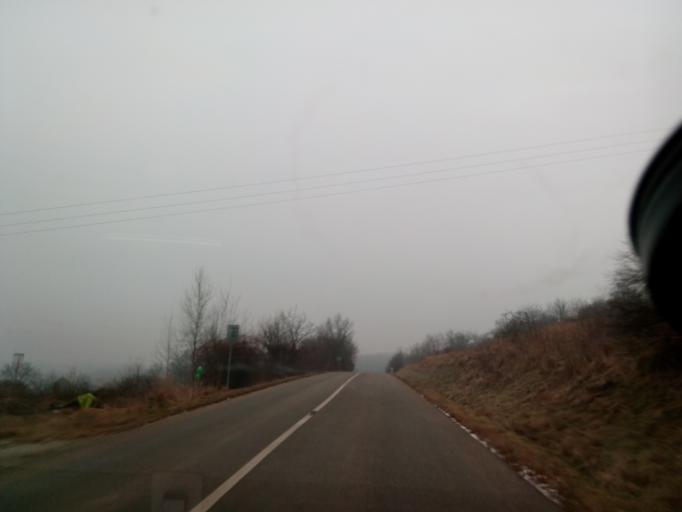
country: SK
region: Kosicky
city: Kosice
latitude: 48.7072
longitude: 21.1544
